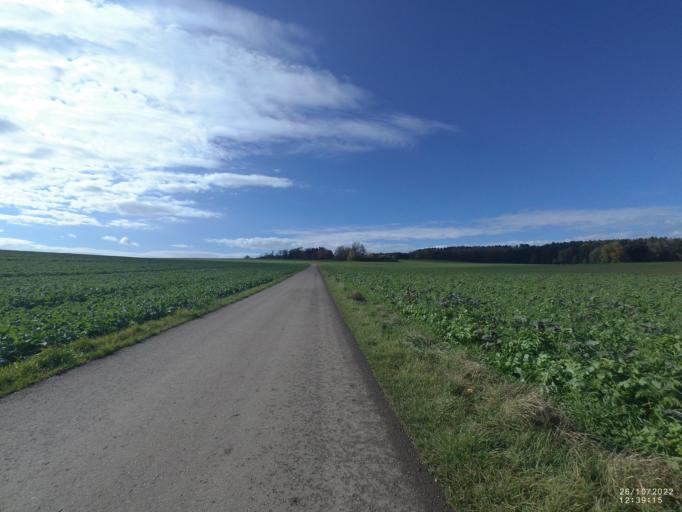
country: DE
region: Baden-Wuerttemberg
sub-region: Regierungsbezirk Stuttgart
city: Bohmenkirch
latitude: 48.6878
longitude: 9.8725
